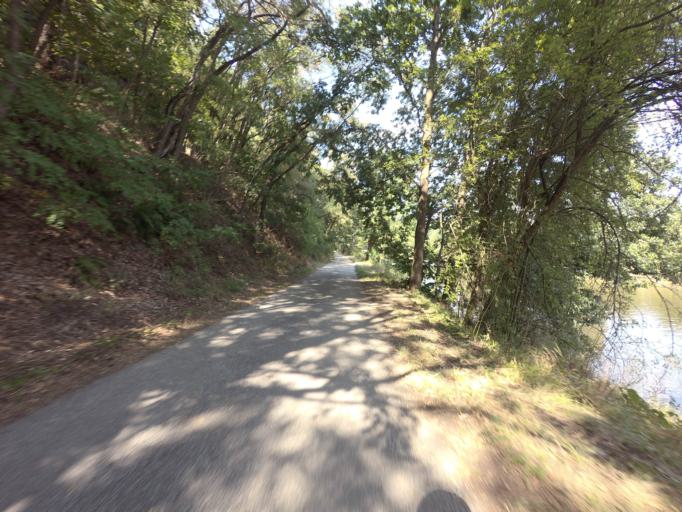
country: CZ
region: Jihocesky
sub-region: Okres Ceske Budejovice
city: Hluboka nad Vltavou
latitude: 49.0591
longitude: 14.4424
